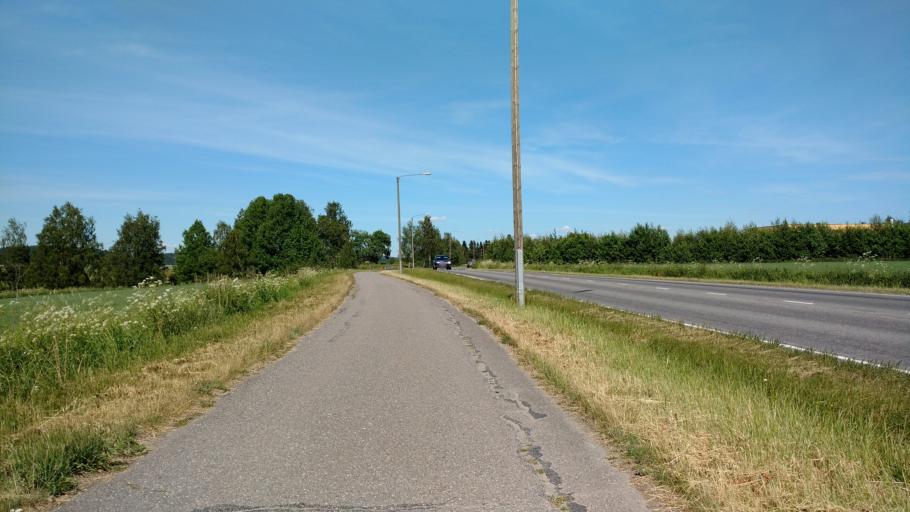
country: FI
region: Varsinais-Suomi
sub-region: Salo
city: Salo
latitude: 60.3971
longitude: 23.1558
